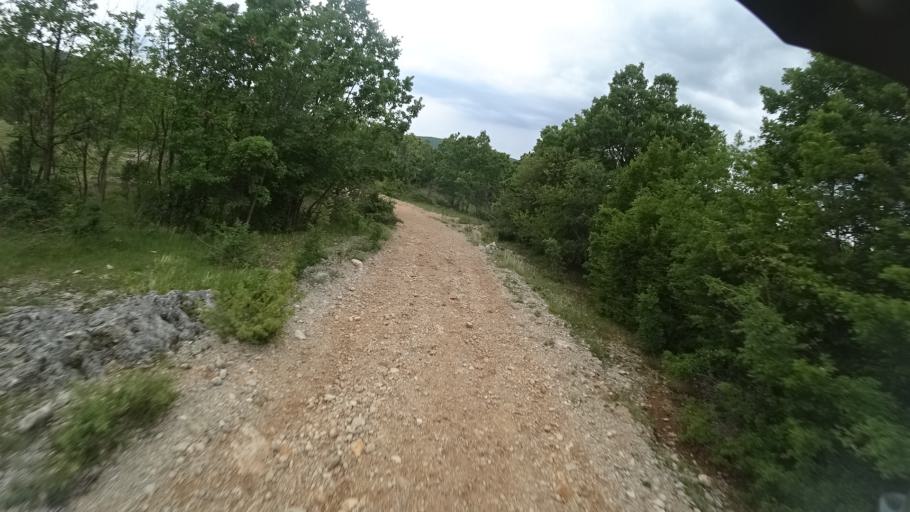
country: HR
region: Sibensko-Kniniska
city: Knin
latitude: 43.9884
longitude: 16.3179
